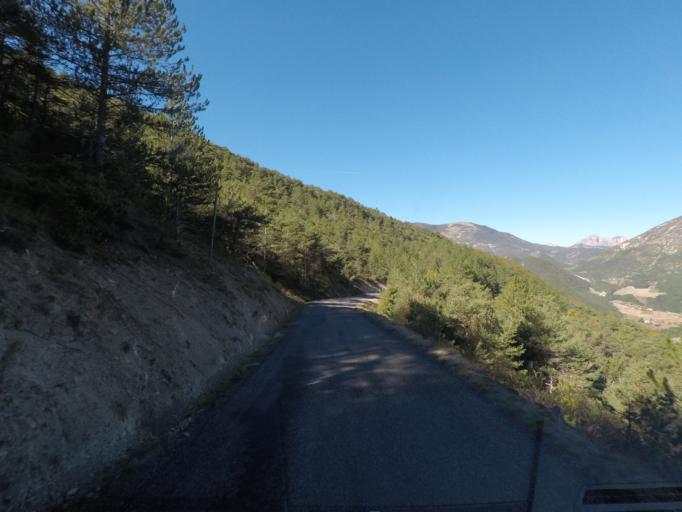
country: FR
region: Rhone-Alpes
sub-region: Departement de la Drome
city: Die
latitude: 44.5765
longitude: 5.2937
